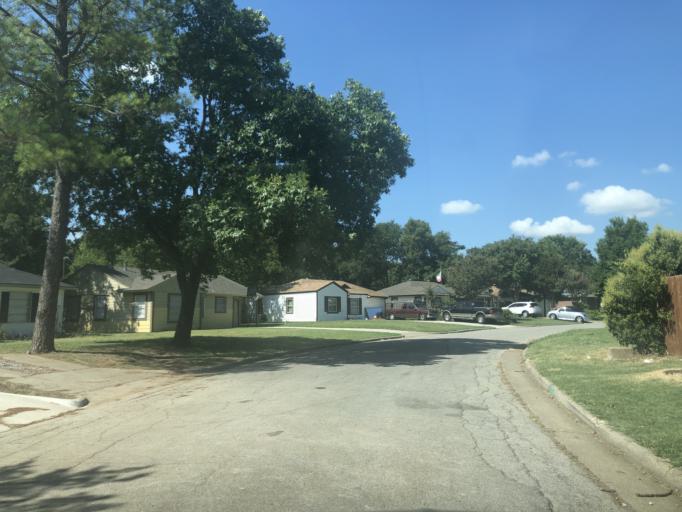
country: US
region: Texas
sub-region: Dallas County
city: Grand Prairie
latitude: 32.7384
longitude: -97.0119
